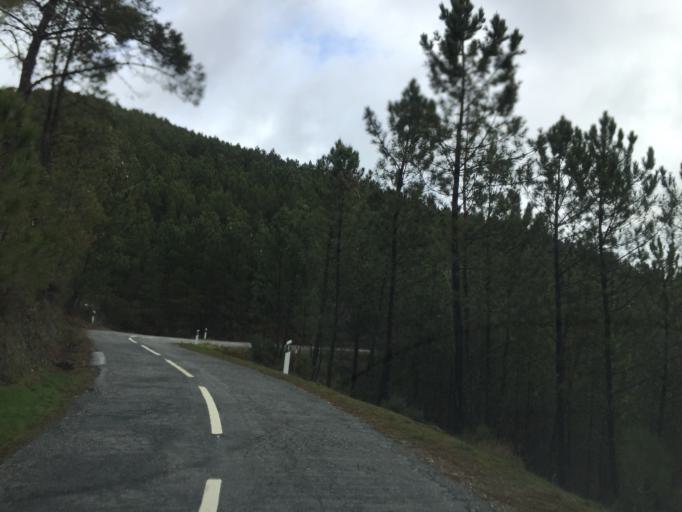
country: PT
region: Guarda
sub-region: Seia
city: Seia
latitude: 40.3265
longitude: -7.7201
